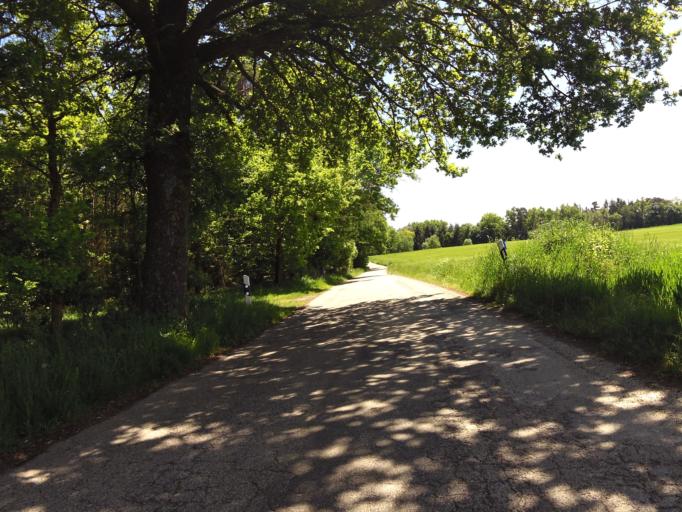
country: DE
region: Bavaria
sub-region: Upper Bavaria
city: Langenbach
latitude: 48.4186
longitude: 11.8330
